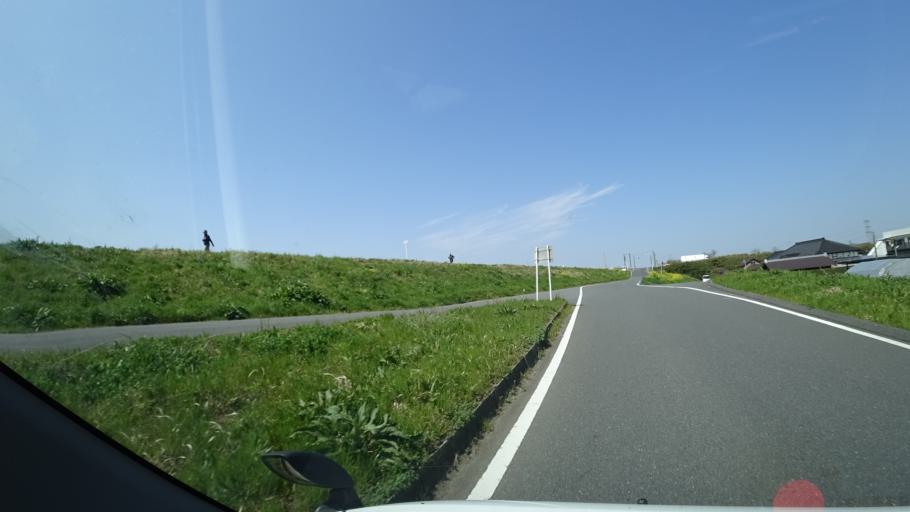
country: JP
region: Ibaraki
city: Edosaki
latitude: 35.8716
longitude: 140.2928
